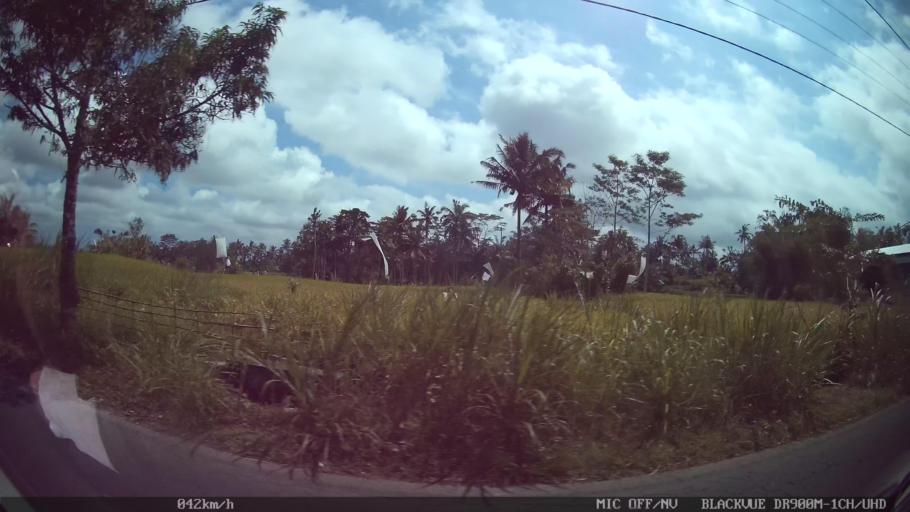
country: ID
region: Bali
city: Banjar Abuan
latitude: -8.4611
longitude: 115.3227
